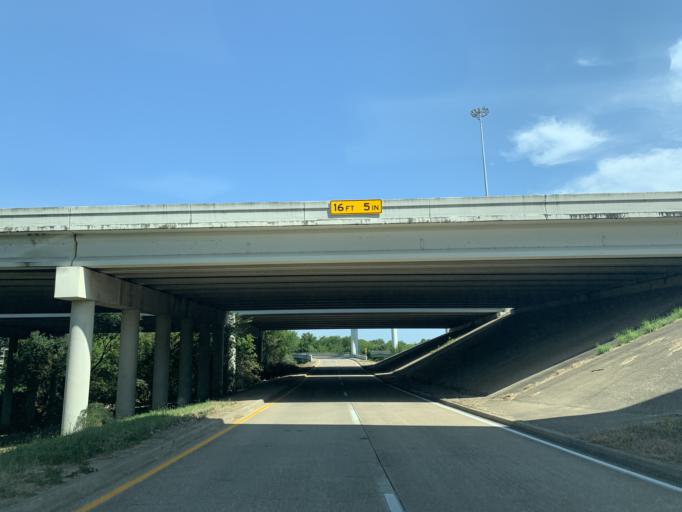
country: US
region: Texas
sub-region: Tarrant County
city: Edgecliff Village
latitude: 32.6672
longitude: -97.3173
